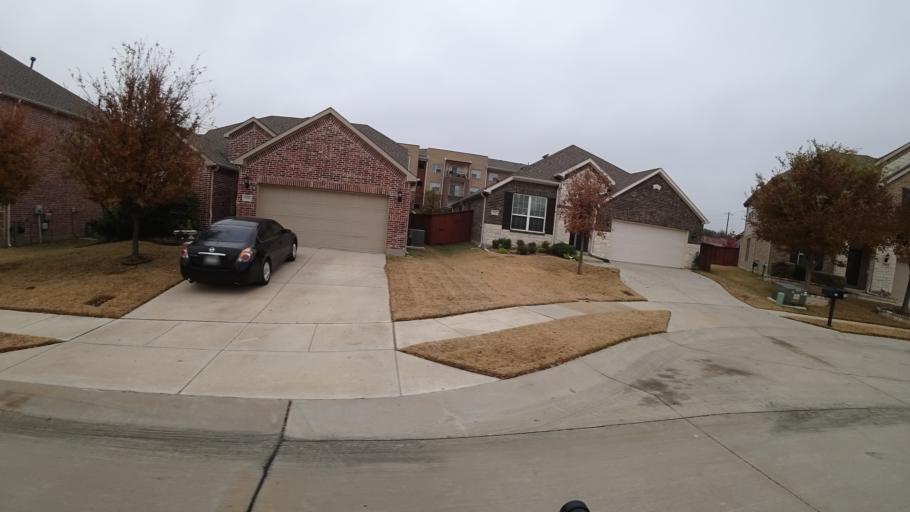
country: US
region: Texas
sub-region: Denton County
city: The Colony
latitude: 33.0634
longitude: -96.9091
